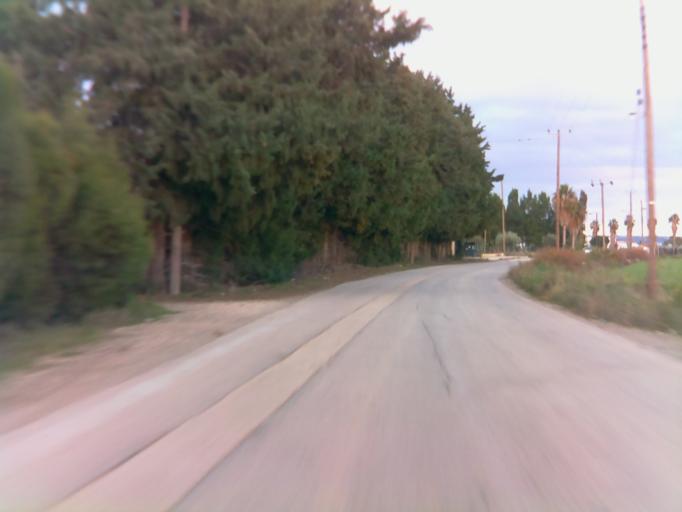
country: CY
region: Pafos
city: Pegeia
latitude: 34.8637
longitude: 32.3546
